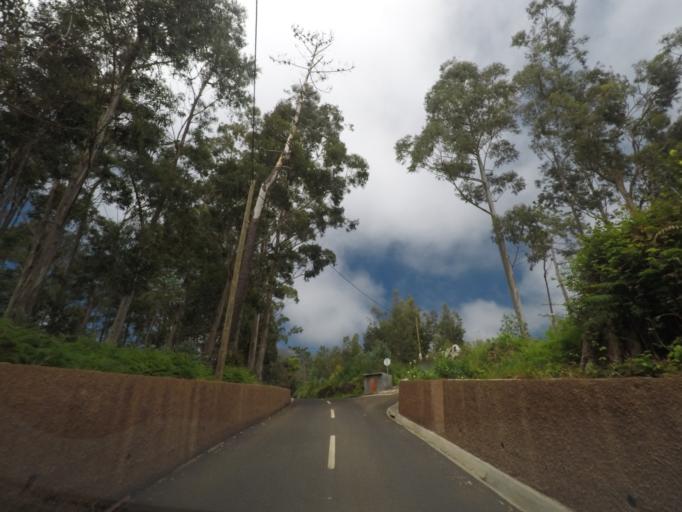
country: PT
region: Madeira
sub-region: Calheta
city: Arco da Calheta
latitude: 32.7205
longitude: -17.1238
